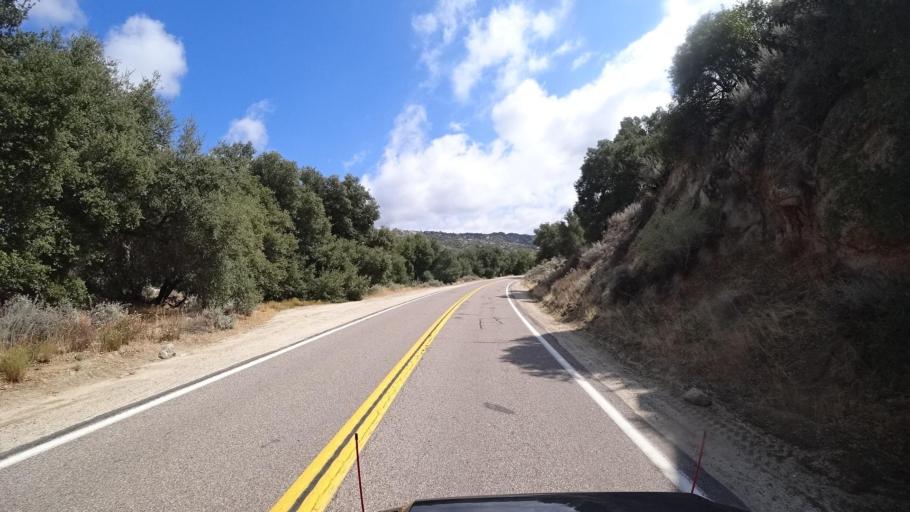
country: US
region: California
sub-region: San Diego County
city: Campo
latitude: 32.7130
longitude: -116.4953
